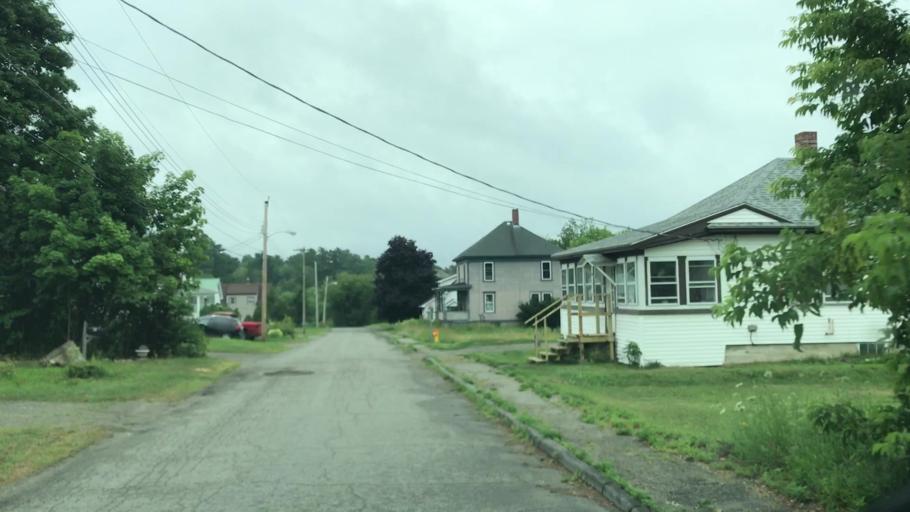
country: US
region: Maine
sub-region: Penobscot County
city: Lincoln
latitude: 45.3663
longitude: -68.4974
